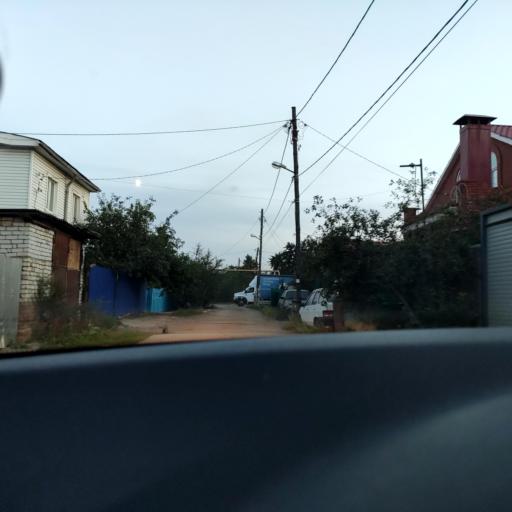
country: RU
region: Samara
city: Smyshlyayevka
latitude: 53.2326
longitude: 50.3029
